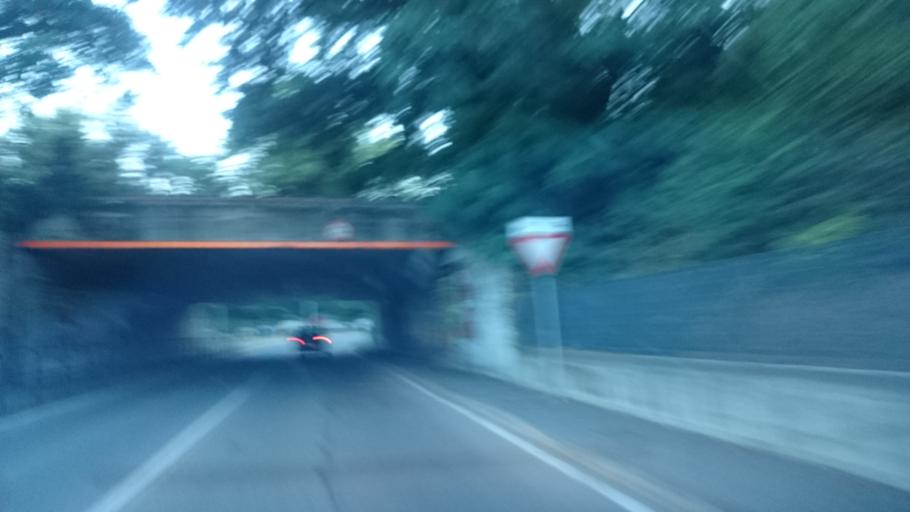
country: IT
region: Emilia-Romagna
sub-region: Provincia di Reggio Emilia
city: Scandiano
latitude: 44.6032
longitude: 10.6894
